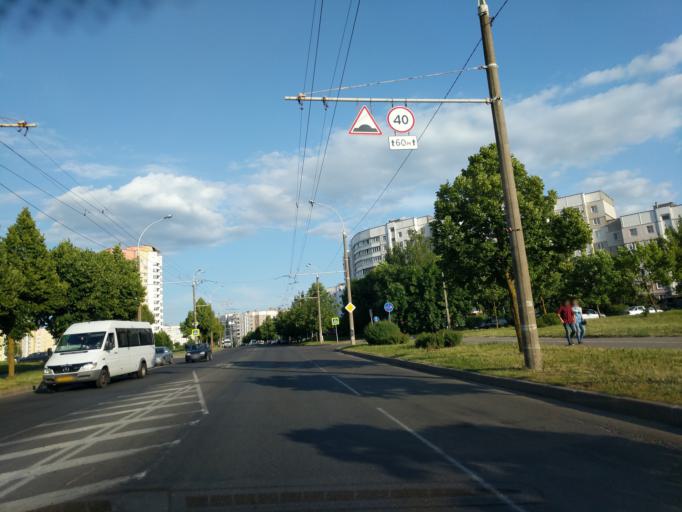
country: BY
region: Minsk
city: Malinovka
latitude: 53.8532
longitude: 27.4485
